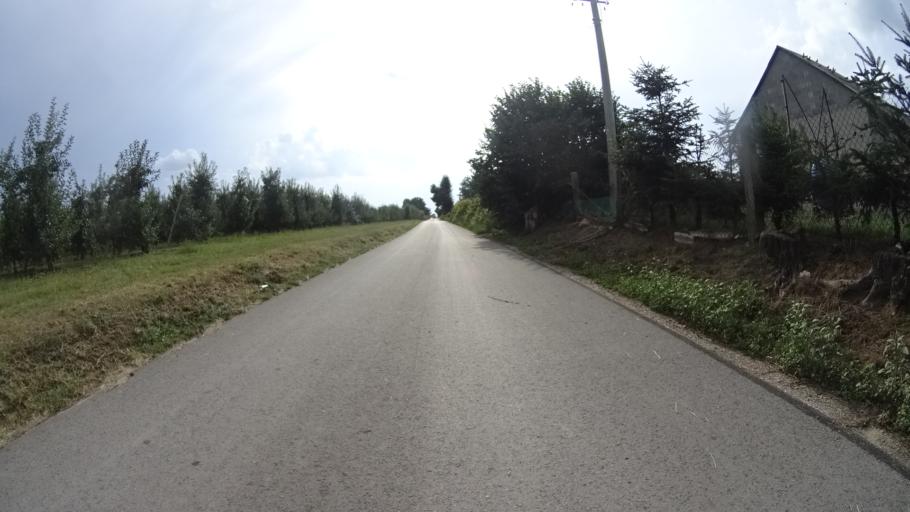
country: PL
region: Masovian Voivodeship
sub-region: Powiat grojecki
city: Goszczyn
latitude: 51.7053
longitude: 20.8437
